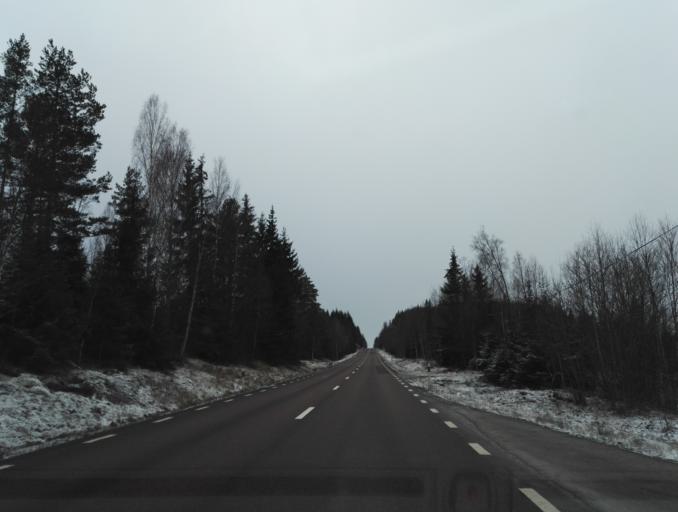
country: SE
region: Kalmar
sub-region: Hultsfreds Kommun
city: Virserum
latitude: 57.2334
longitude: 15.5384
